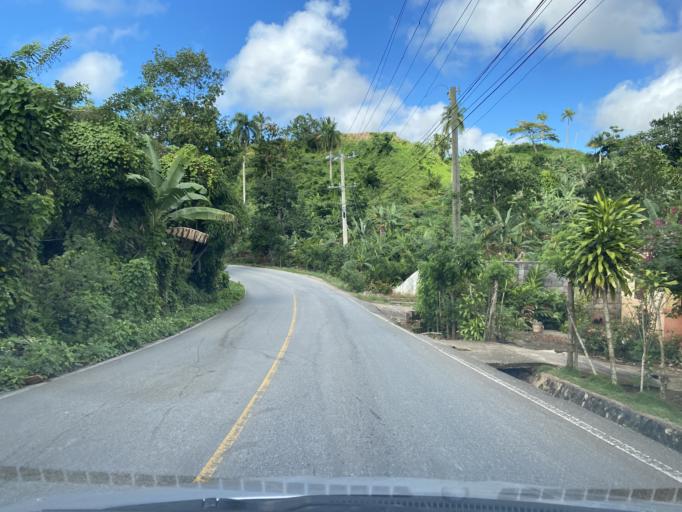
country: DO
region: Samana
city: Las Terrenas
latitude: 19.2794
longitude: -69.5533
